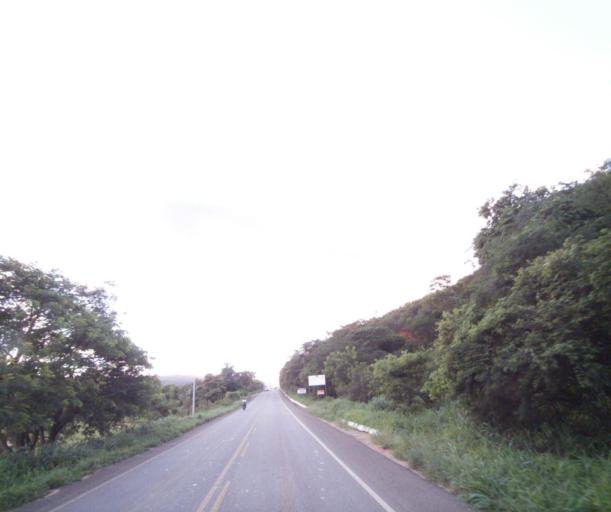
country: BR
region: Bahia
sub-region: Caetite
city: Caetite
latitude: -14.0666
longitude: -42.4686
